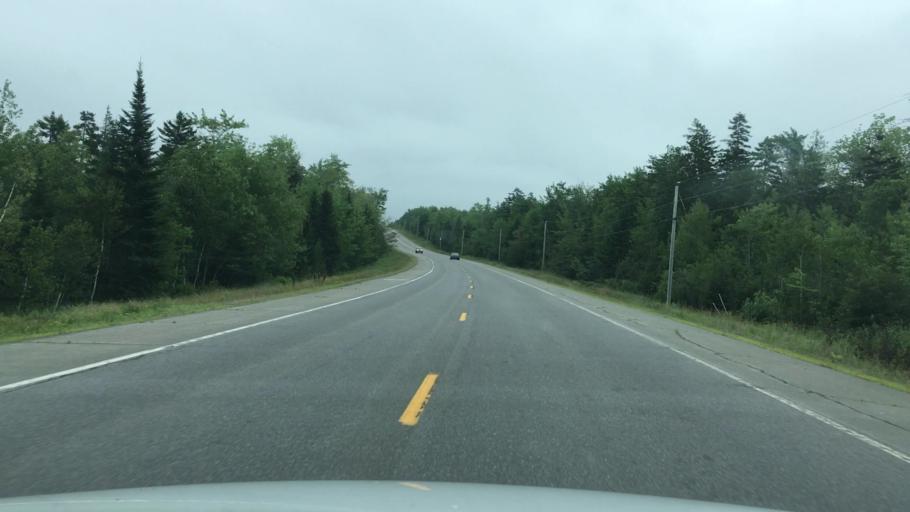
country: US
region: Maine
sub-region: Hancock County
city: Franklin
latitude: 44.8304
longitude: -68.1321
